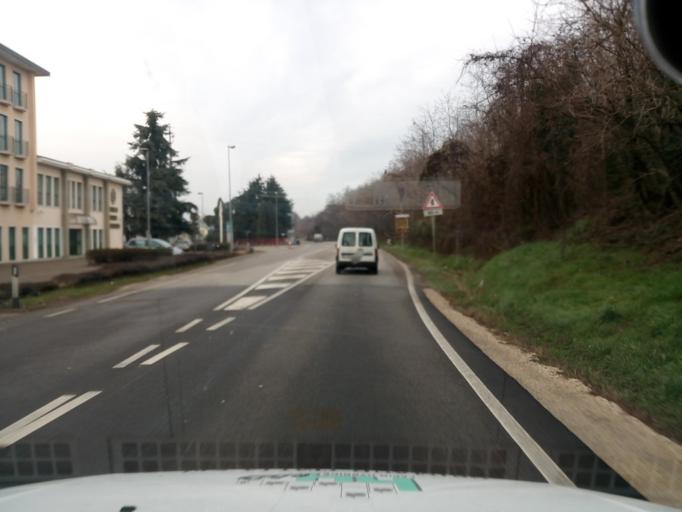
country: IT
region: Veneto
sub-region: Provincia di Vicenza
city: Zermeghedo
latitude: 45.4768
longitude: 11.3819
